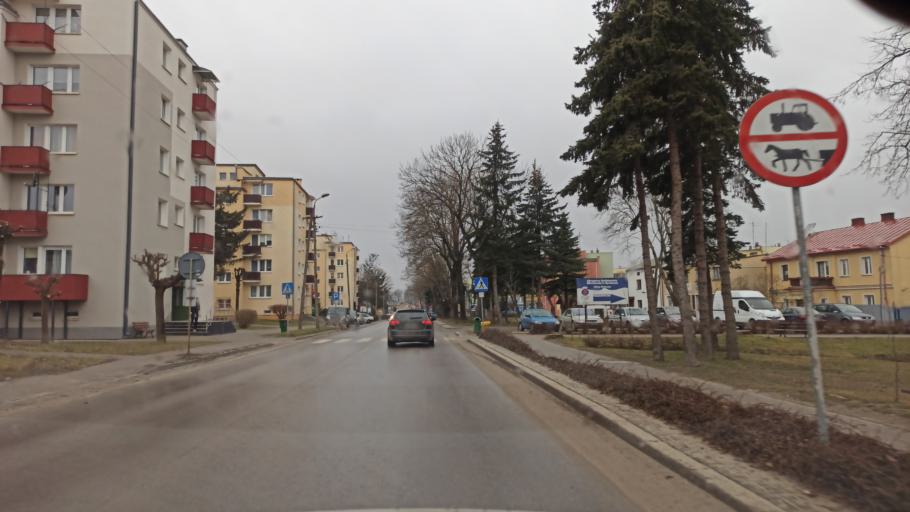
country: PL
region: Lublin Voivodeship
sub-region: Powiat lubelski
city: Bychawa
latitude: 51.0127
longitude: 22.5404
